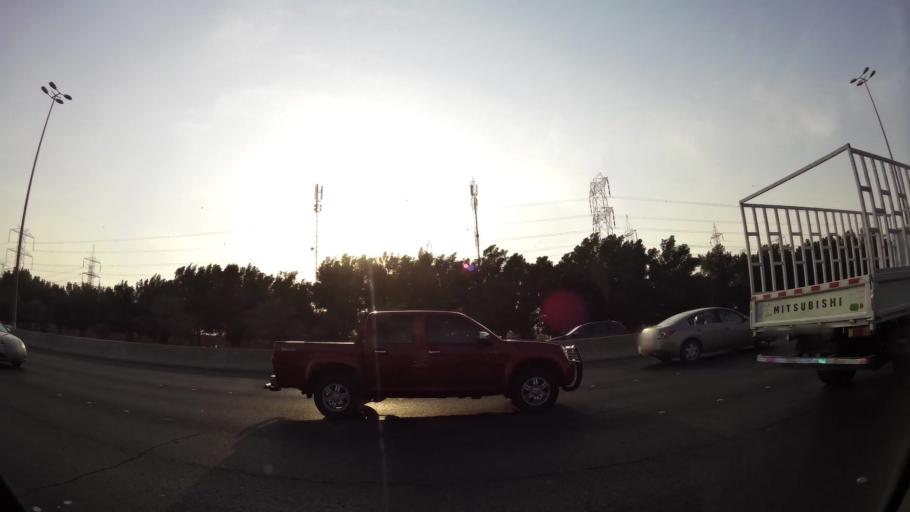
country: KW
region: Mubarak al Kabir
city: Sabah as Salim
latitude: 29.2320
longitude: 48.0523
